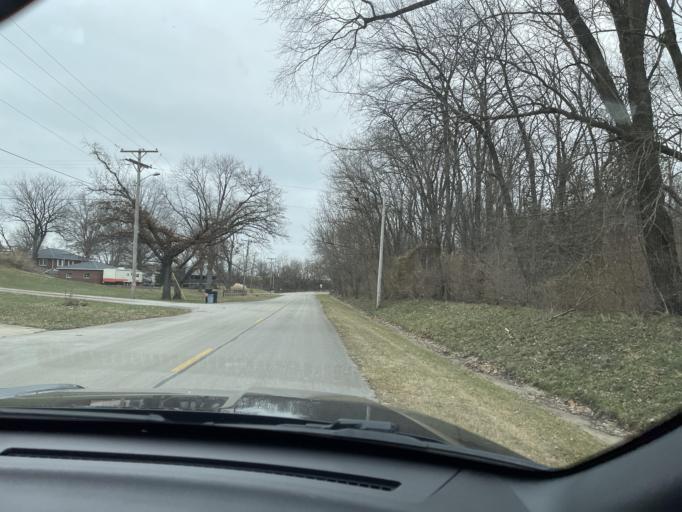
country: US
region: Illinois
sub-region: Sangamon County
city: Grandview
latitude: 39.7999
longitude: -89.5992
